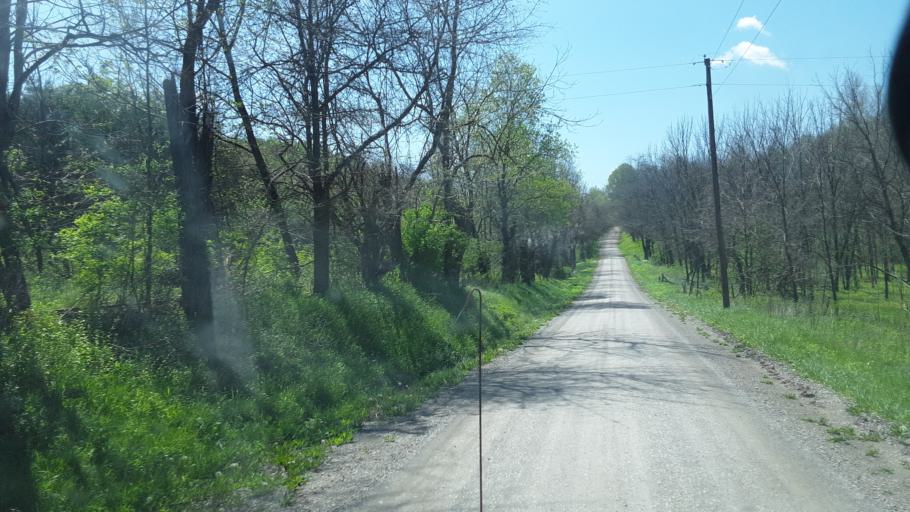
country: US
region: Ohio
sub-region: Noble County
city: Caldwell
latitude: 39.7657
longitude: -81.5876
